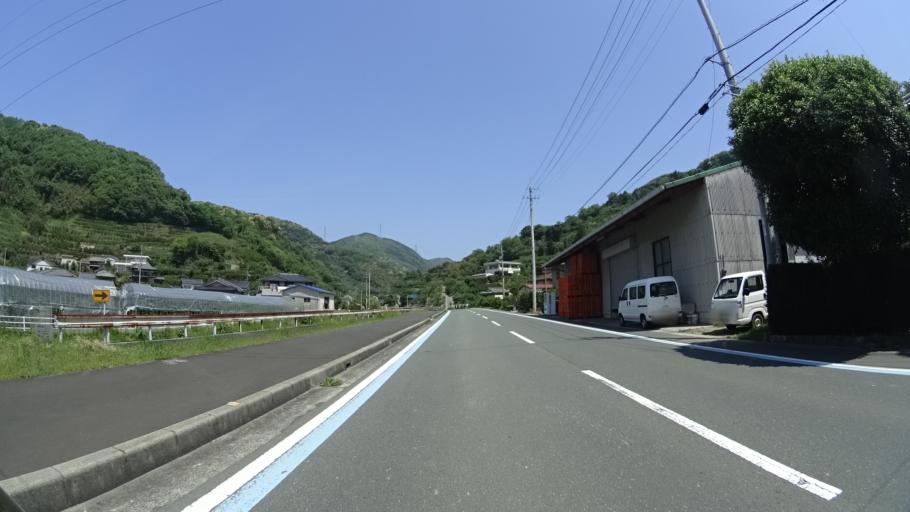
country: JP
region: Ehime
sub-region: Nishiuwa-gun
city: Ikata-cho
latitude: 33.4970
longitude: 132.3972
